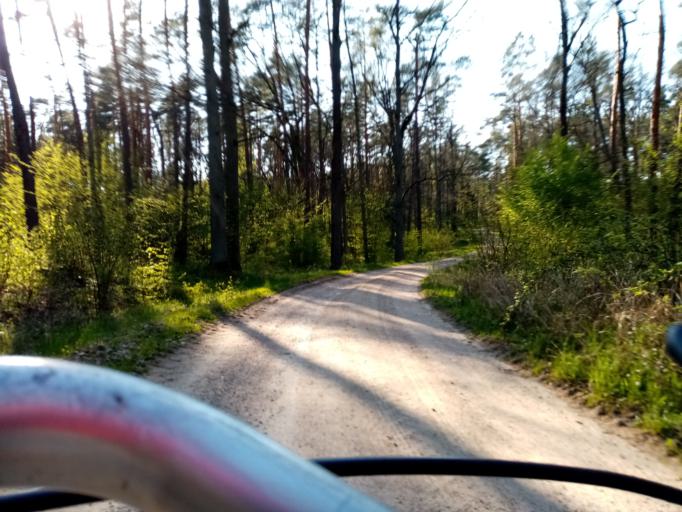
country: PL
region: Kujawsko-Pomorskie
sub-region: Powiat brodnicki
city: Gorzno
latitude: 53.1618
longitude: 19.6807
